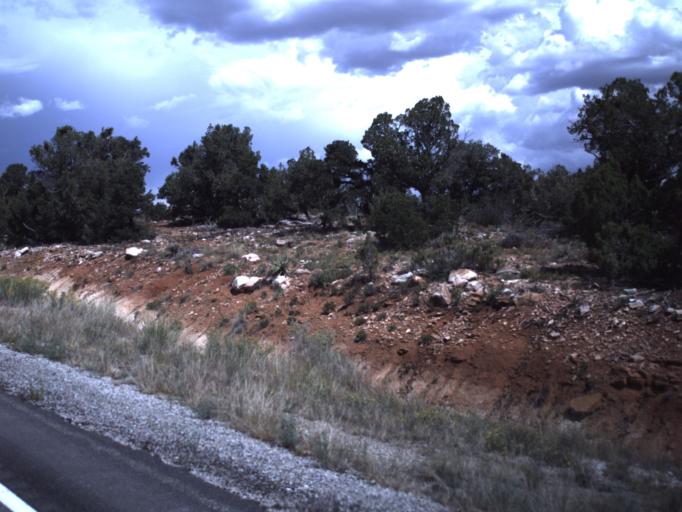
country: US
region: Utah
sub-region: San Juan County
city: Blanding
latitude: 37.6875
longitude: -109.4322
